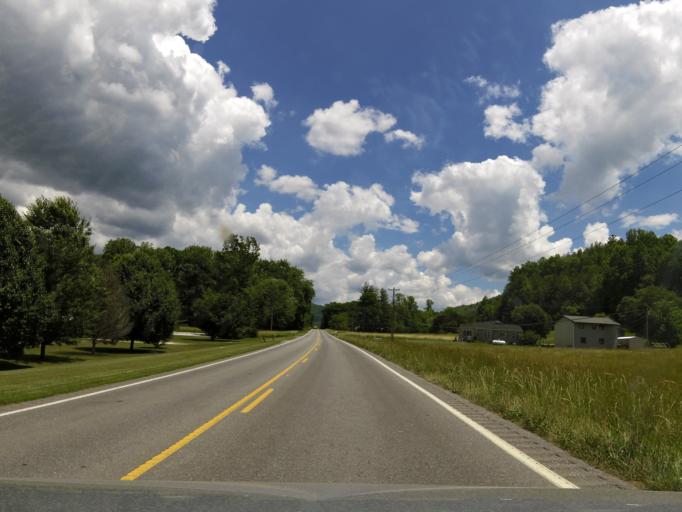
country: US
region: North Carolina
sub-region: Graham County
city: Robbinsville
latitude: 35.2955
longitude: -83.7909
